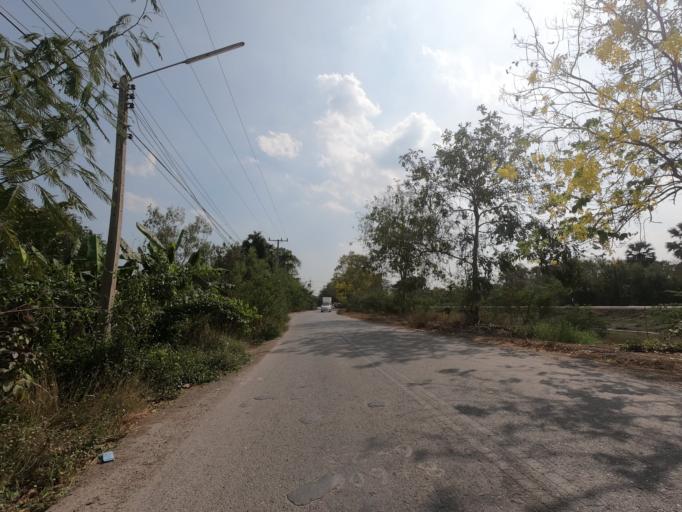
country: TH
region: Pathum Thani
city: Nong Suea
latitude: 14.1382
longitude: 100.8464
